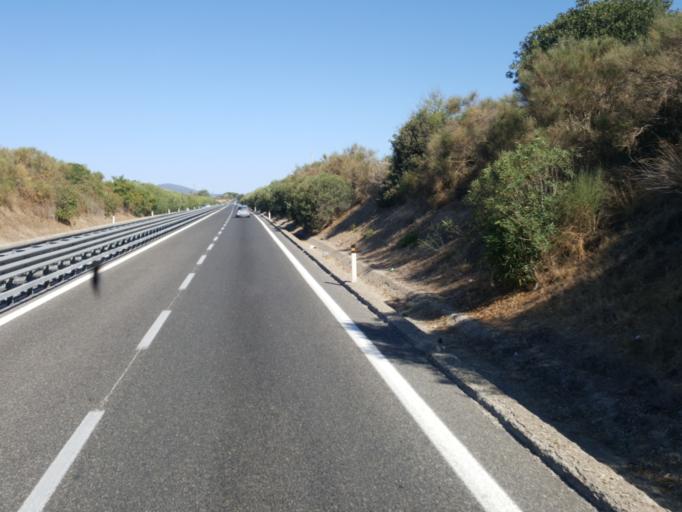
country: IT
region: Latium
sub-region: Provincia di Viterbo
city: Pescia Romana
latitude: 42.3805
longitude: 11.5522
